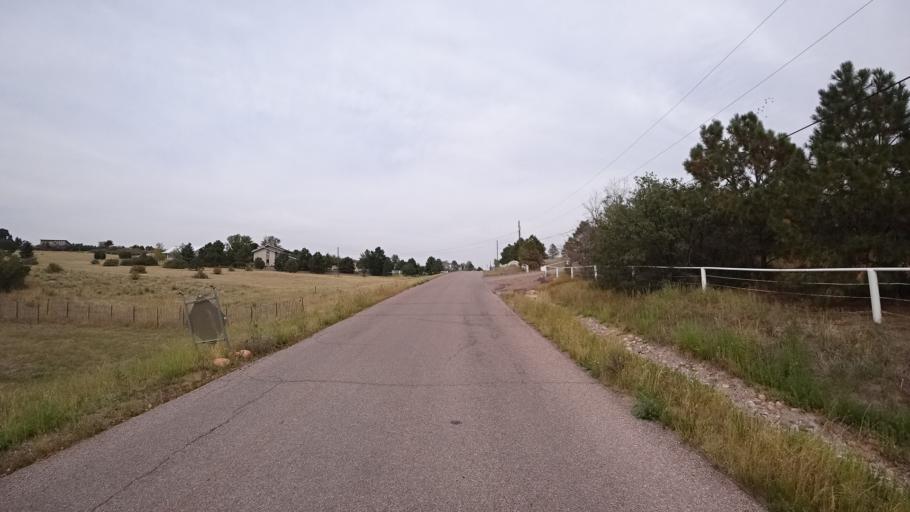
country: US
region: Colorado
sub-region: El Paso County
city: Cimarron Hills
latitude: 38.8968
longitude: -104.7245
